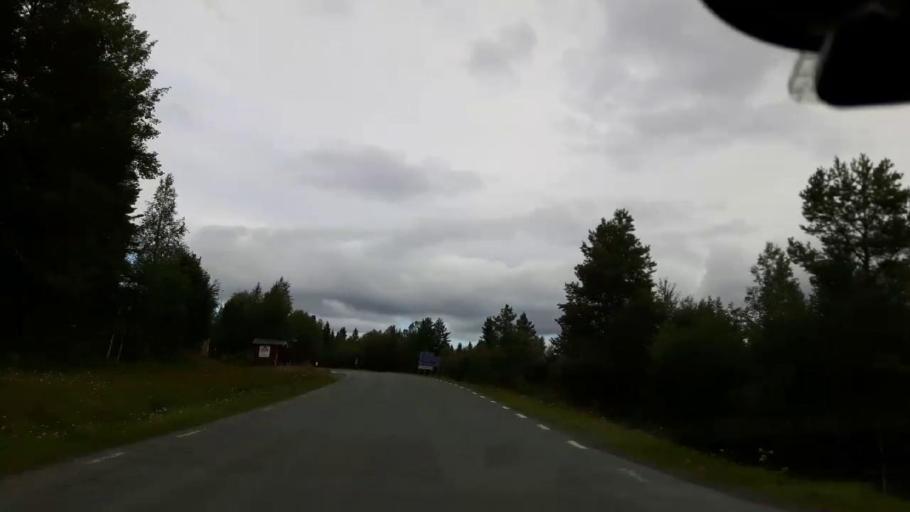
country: SE
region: Jaemtland
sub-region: Krokoms Kommun
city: Valla
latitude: 63.5694
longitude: 13.8402
